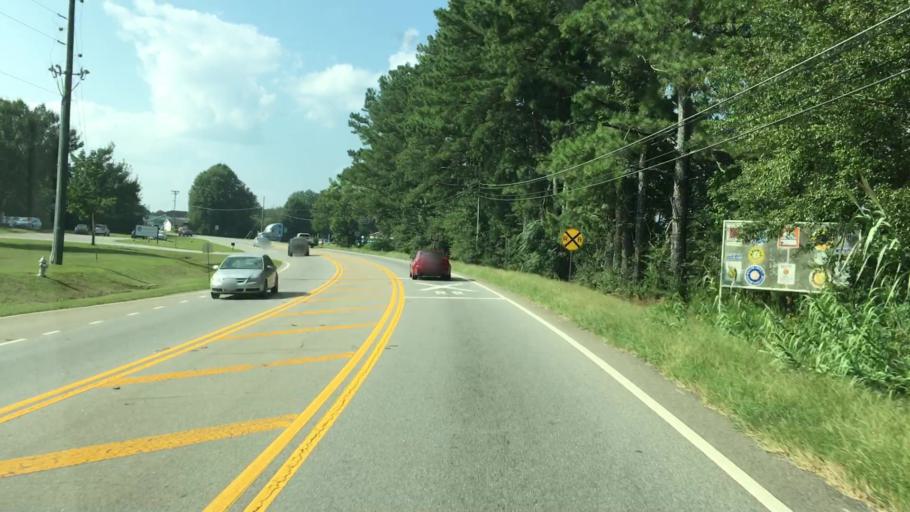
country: US
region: Georgia
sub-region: Walton County
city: Monroe
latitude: 33.7688
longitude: -83.6998
